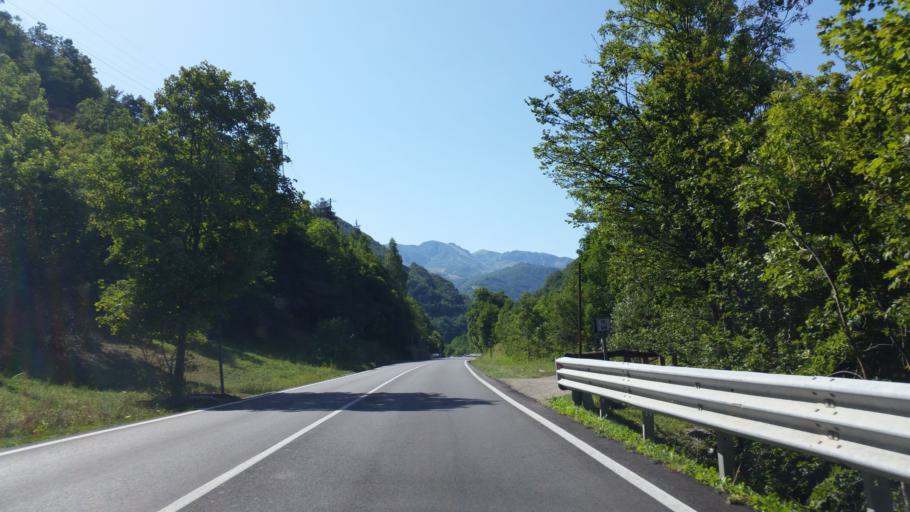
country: IT
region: Piedmont
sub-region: Provincia di Cuneo
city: Limone Piemonte
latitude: 44.2210
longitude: 7.5683
